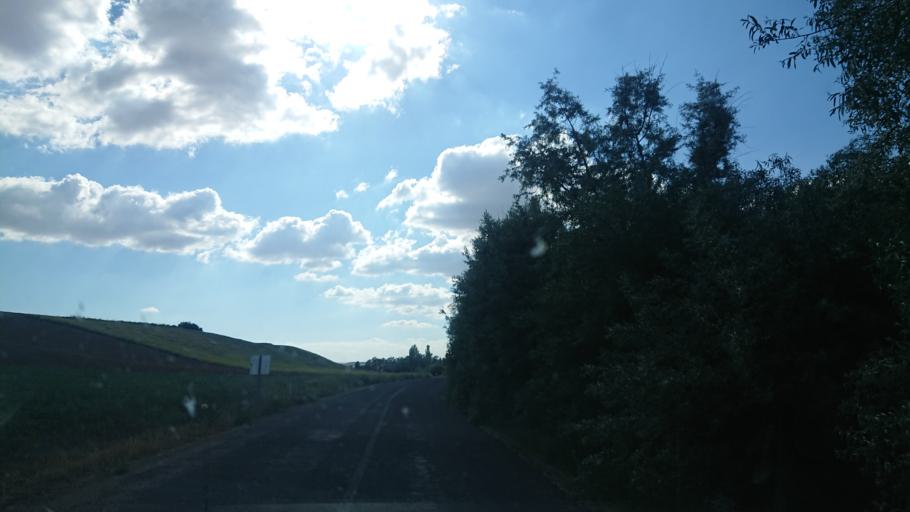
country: TR
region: Aksaray
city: Agacoren
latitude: 38.7577
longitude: 33.9108
